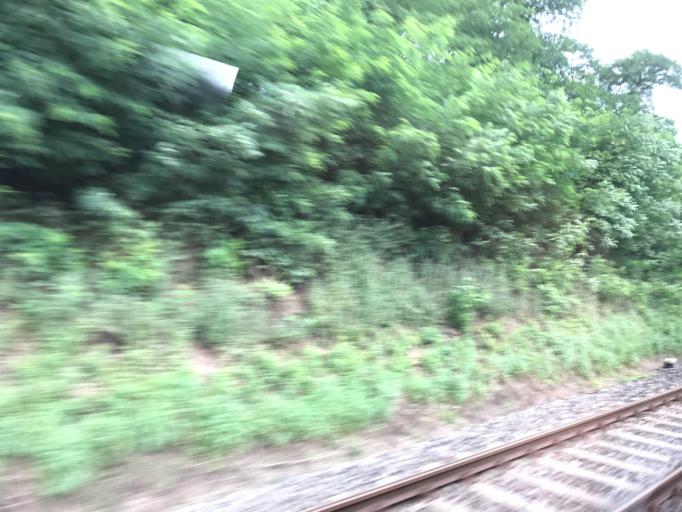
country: DE
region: Hesse
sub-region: Regierungsbezirk Giessen
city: Steeden
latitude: 50.3966
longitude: 8.1190
